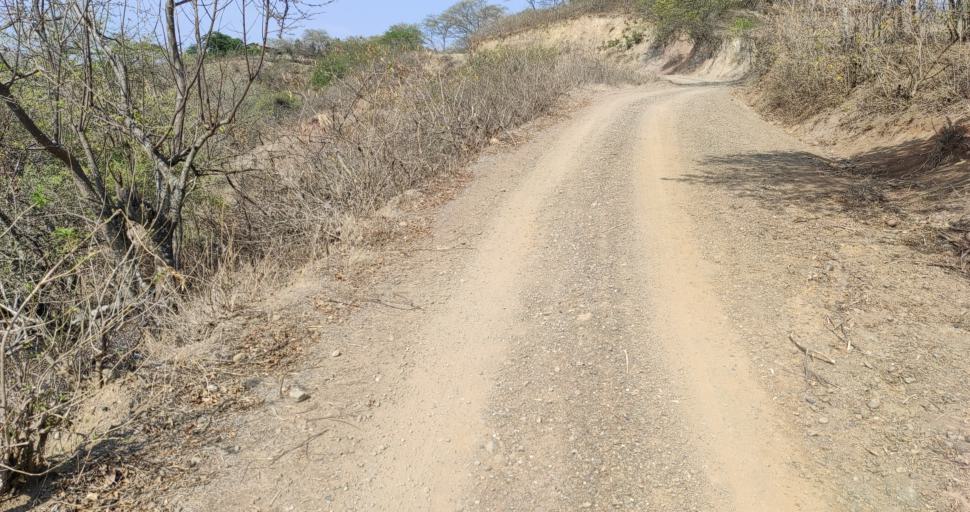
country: EC
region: Loja
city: Catacocha
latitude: -4.0066
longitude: -79.7112
